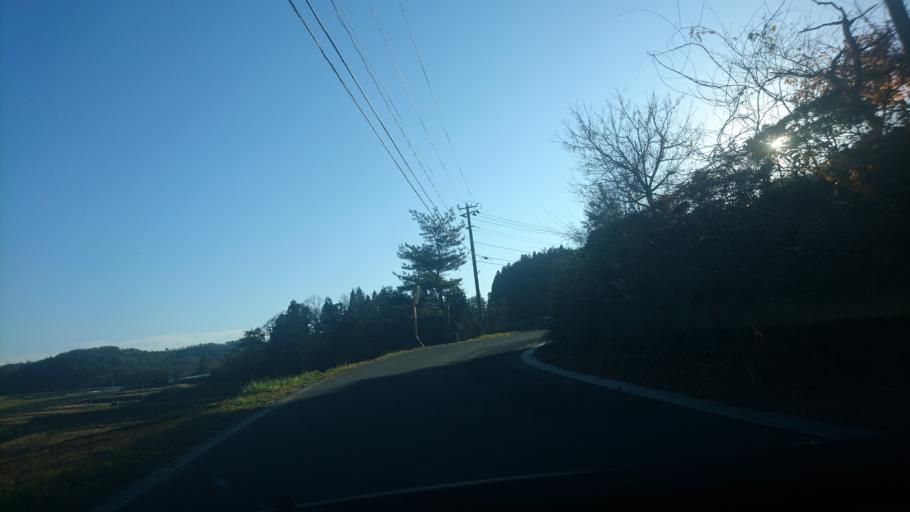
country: JP
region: Iwate
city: Ichinoseki
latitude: 38.9059
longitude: 141.2226
